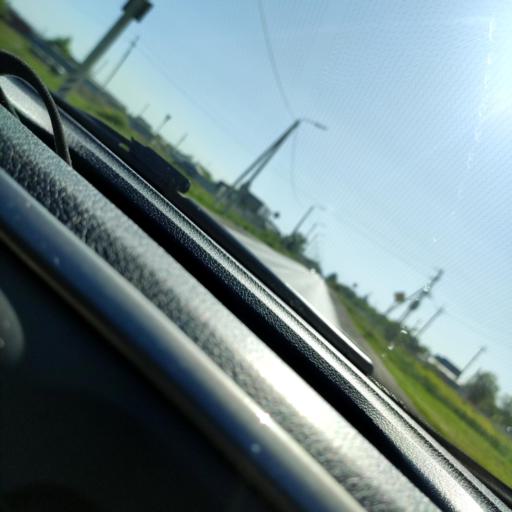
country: RU
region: Samara
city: Podstepki
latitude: 53.5233
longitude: 49.1673
